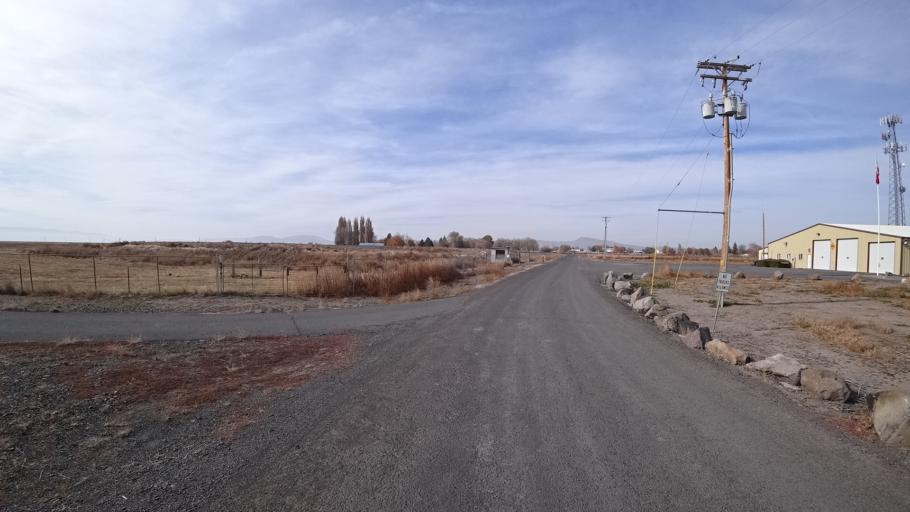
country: US
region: California
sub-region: Siskiyou County
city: Tulelake
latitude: 41.9492
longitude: -121.4685
